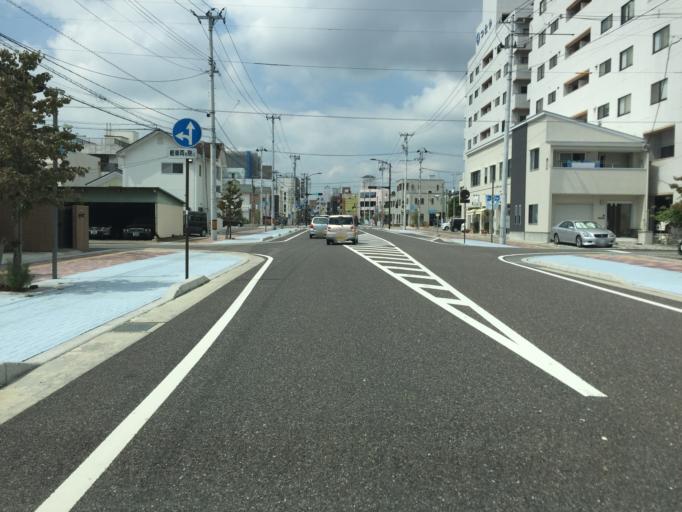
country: JP
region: Fukushima
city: Koriyama
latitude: 37.3931
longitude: 140.3844
